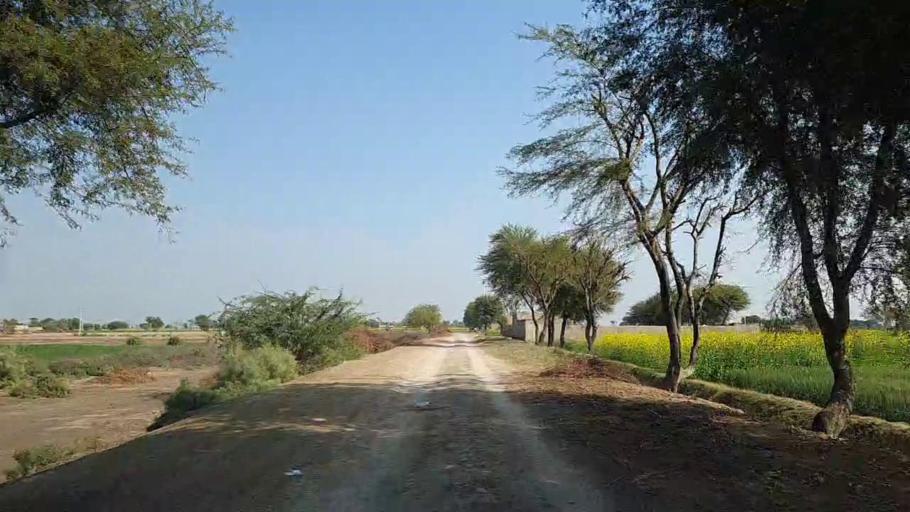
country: PK
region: Sindh
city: Jam Sahib
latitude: 26.2540
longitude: 68.5698
